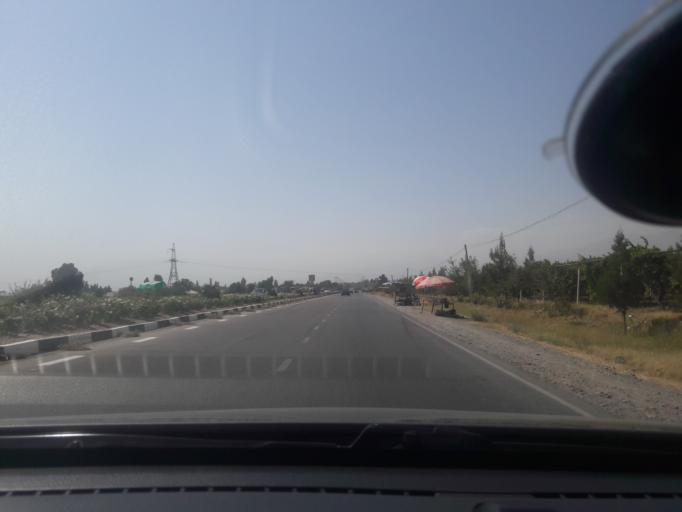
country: TJ
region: Republican Subordination
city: Hisor
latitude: 38.5600
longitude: 68.4546
